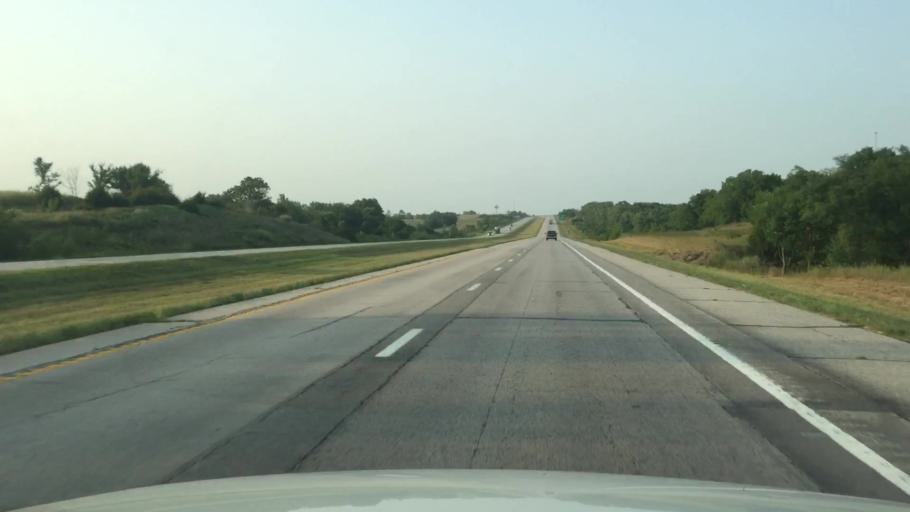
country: US
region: Missouri
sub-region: Harrison County
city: Bethany
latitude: 40.4425
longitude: -93.9835
